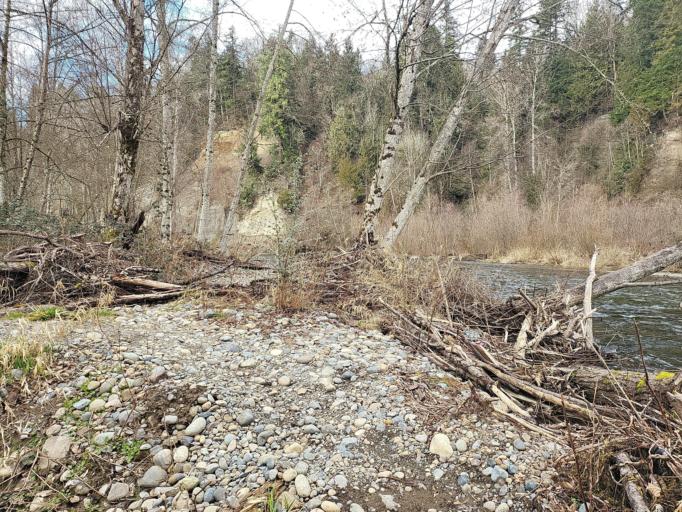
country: US
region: Washington
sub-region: King County
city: Fairwood
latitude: 47.4704
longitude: -122.1527
